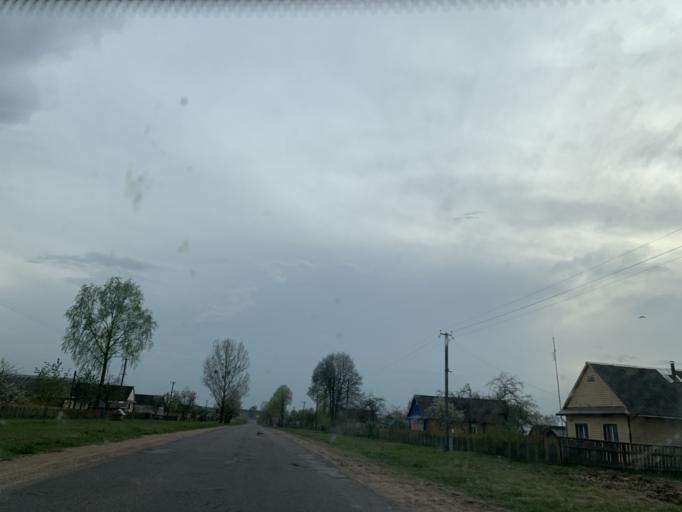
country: BY
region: Minsk
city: Kapyl'
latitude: 53.2726
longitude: 26.9652
